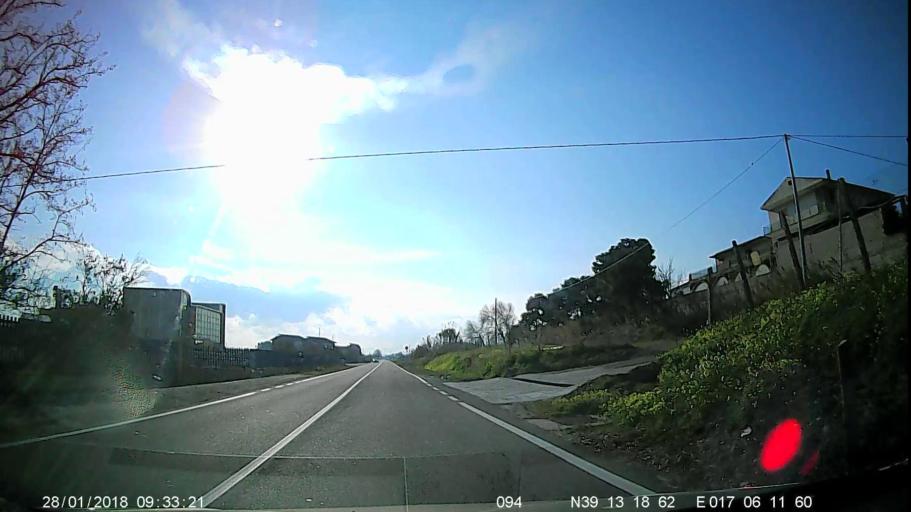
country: IT
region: Calabria
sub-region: Provincia di Crotone
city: Tronca
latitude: 39.2215
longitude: 17.1034
